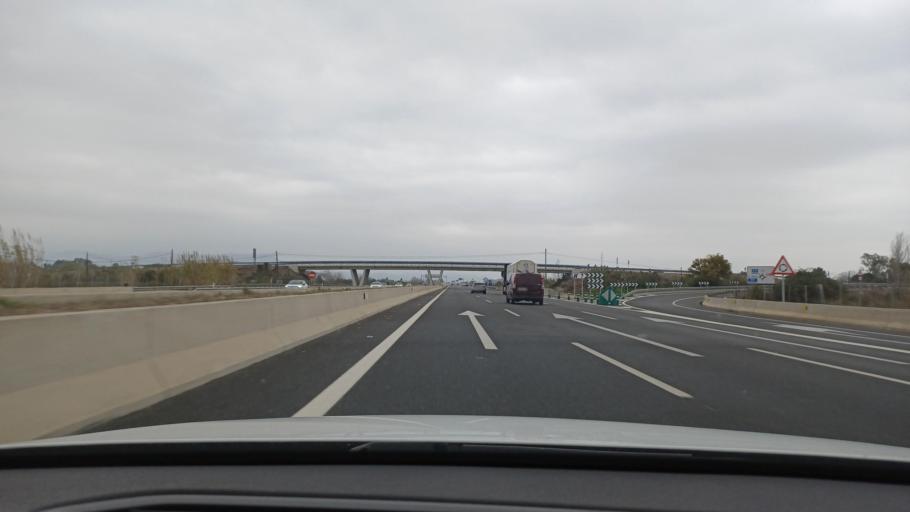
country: ES
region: Valencia
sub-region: Provincia de Valencia
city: Puig
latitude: 39.5666
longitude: -0.2960
